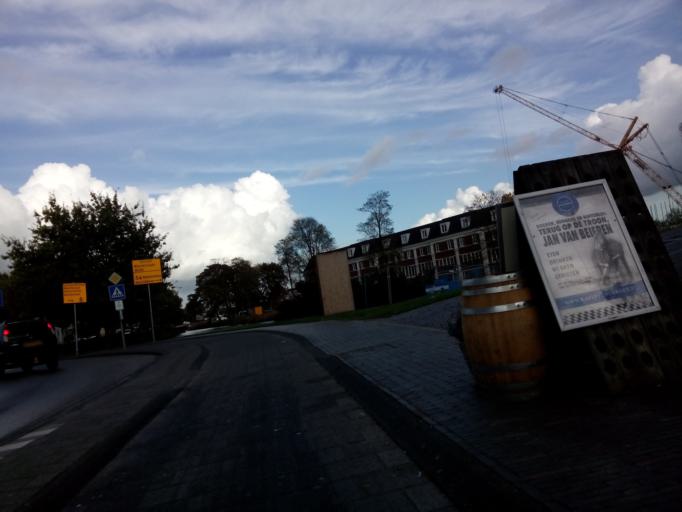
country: NL
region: Utrecht
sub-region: Gemeente Woerden
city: Woerden
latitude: 52.0855
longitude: 4.8878
